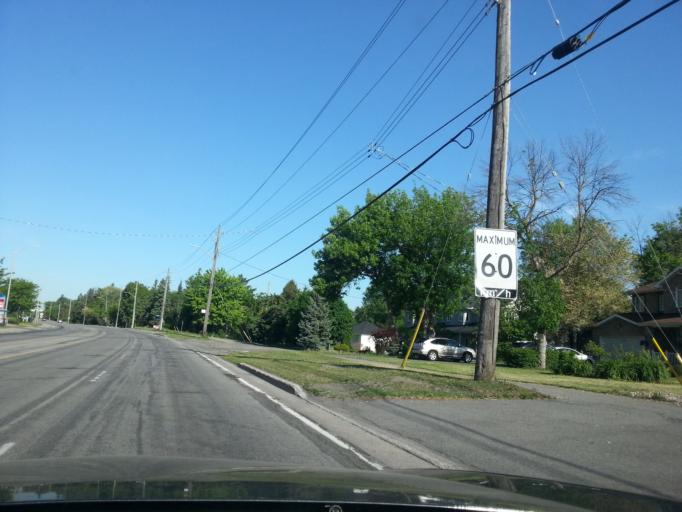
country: CA
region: Ontario
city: Bells Corners
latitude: 45.3523
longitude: -75.8340
